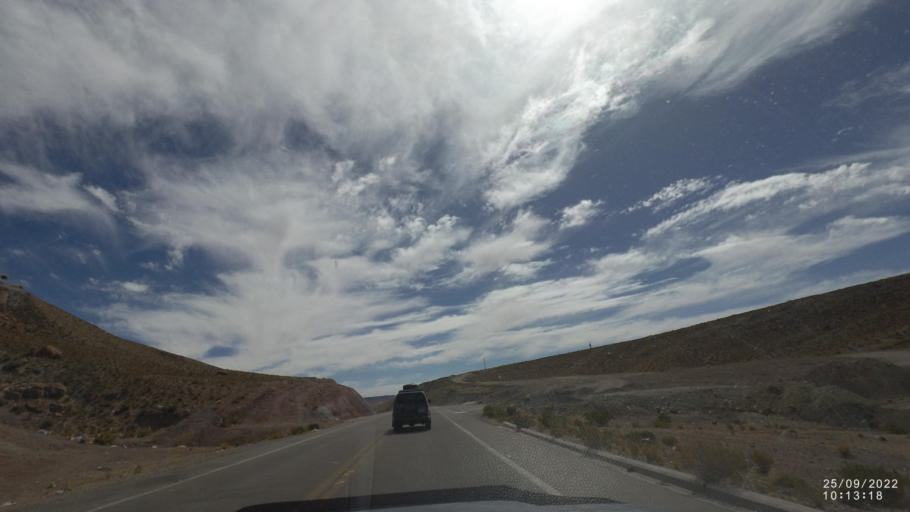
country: BO
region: Potosi
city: Colchani
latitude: -20.0751
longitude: -66.8884
